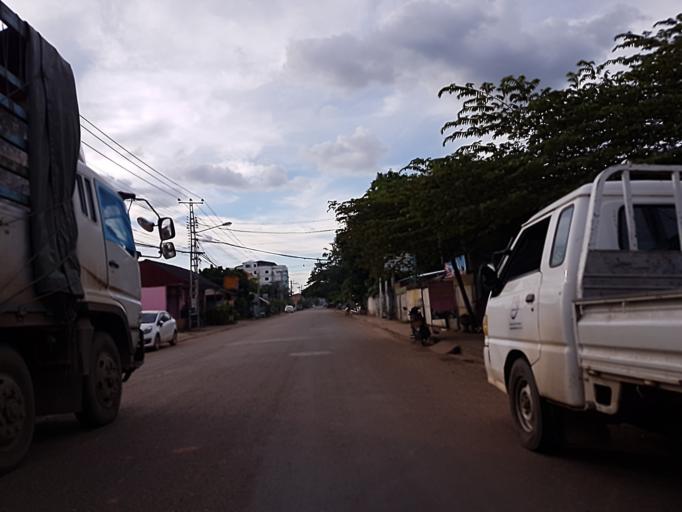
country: LA
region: Vientiane
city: Vientiane
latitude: 17.9771
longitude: 102.5902
